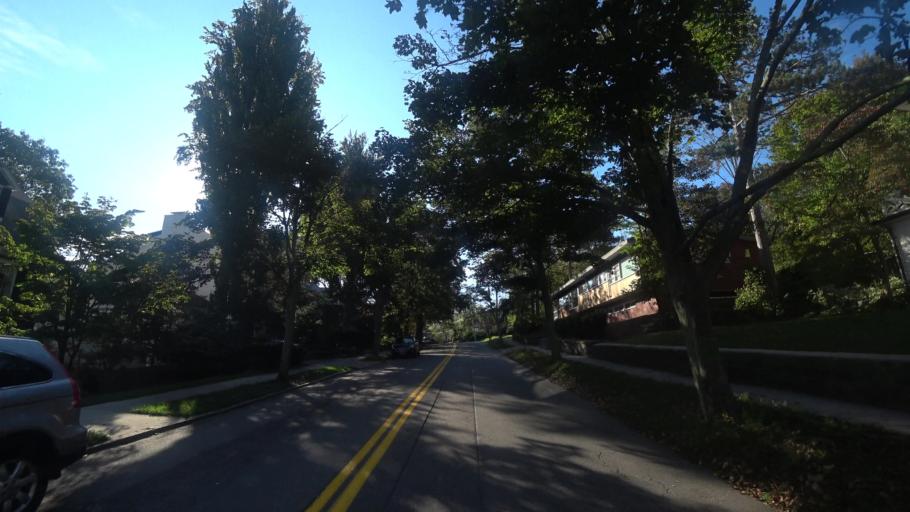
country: US
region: Massachusetts
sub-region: Norfolk County
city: Brookline
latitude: 42.3315
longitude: -71.1351
